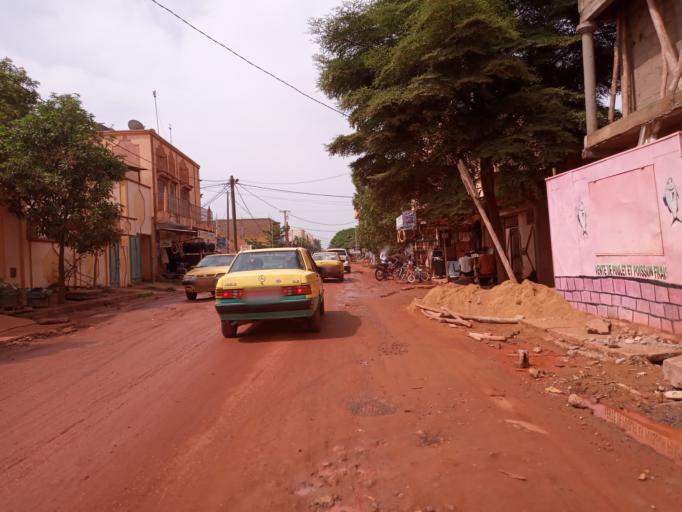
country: ML
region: Bamako
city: Bamako
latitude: 12.5594
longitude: -7.9902
